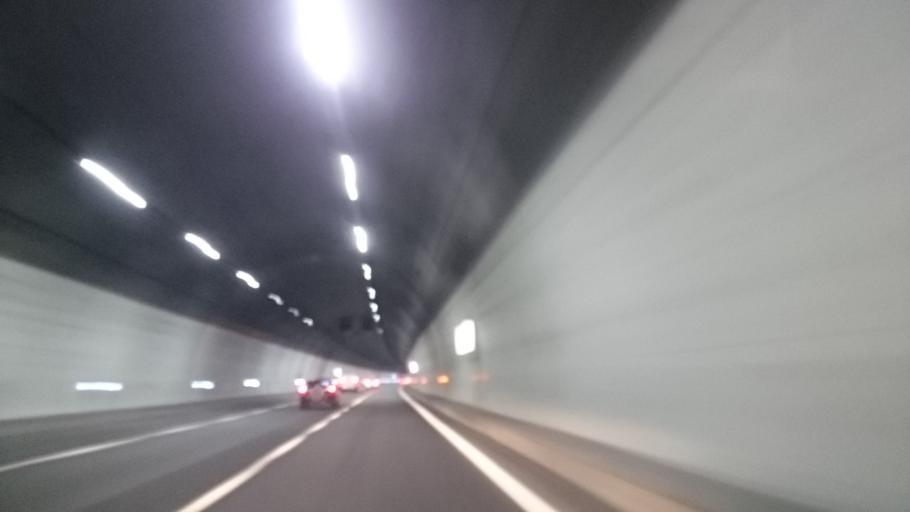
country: IT
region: Emilia-Romagna
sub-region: Provincia di Bologna
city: Vado
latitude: 44.3246
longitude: 11.2555
